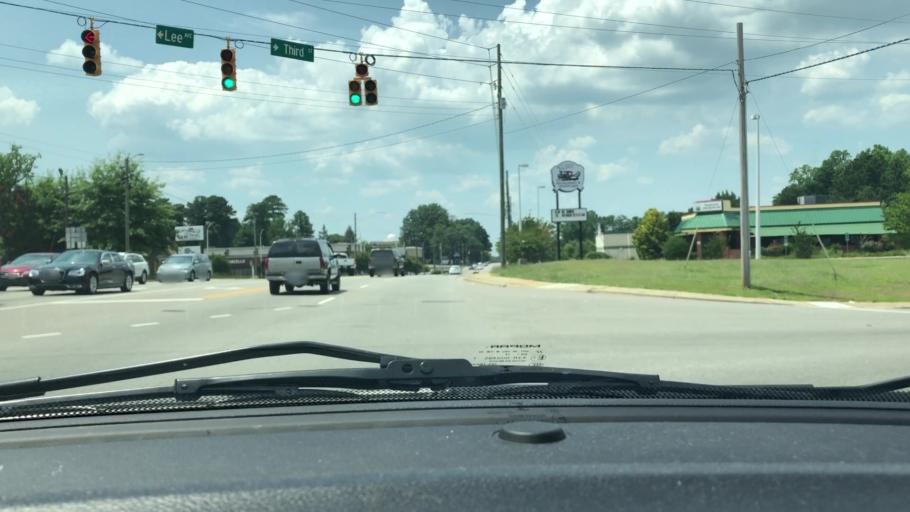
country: US
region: North Carolina
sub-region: Lee County
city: Sanford
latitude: 35.4654
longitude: -79.1586
